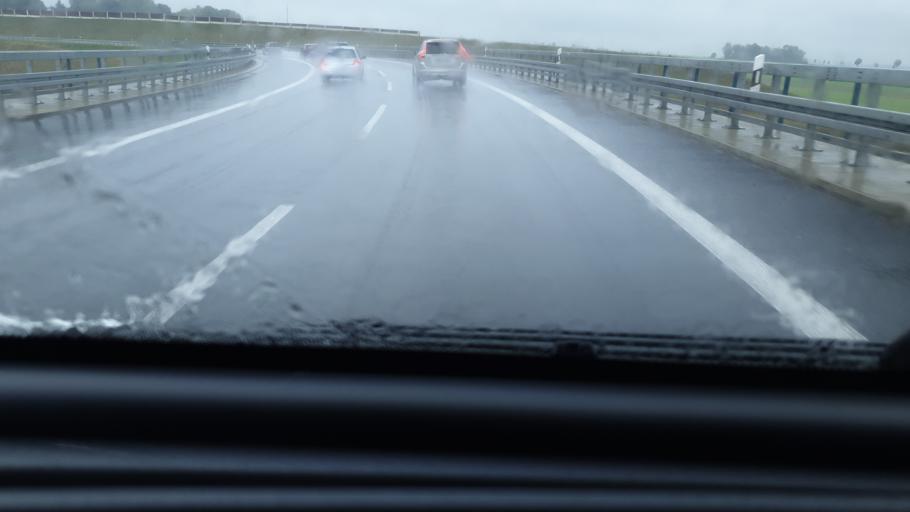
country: DE
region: North Rhine-Westphalia
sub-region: Regierungsbezirk Koln
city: Titz
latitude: 51.0323
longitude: 6.4691
